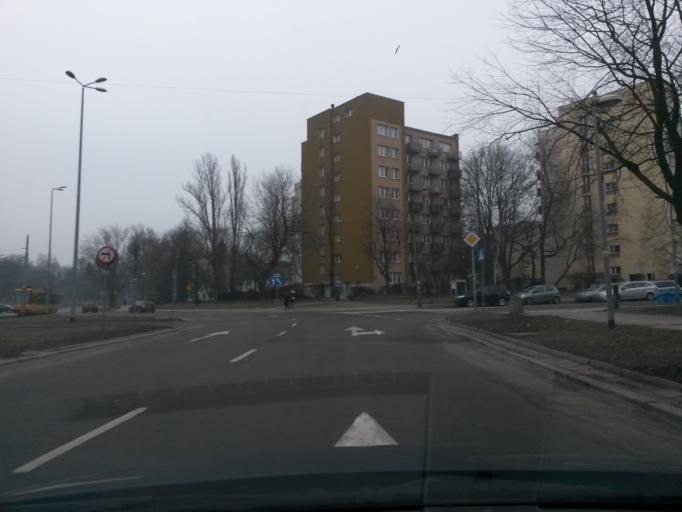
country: PL
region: Masovian Voivodeship
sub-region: Warszawa
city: Wola
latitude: 52.2439
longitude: 20.9666
